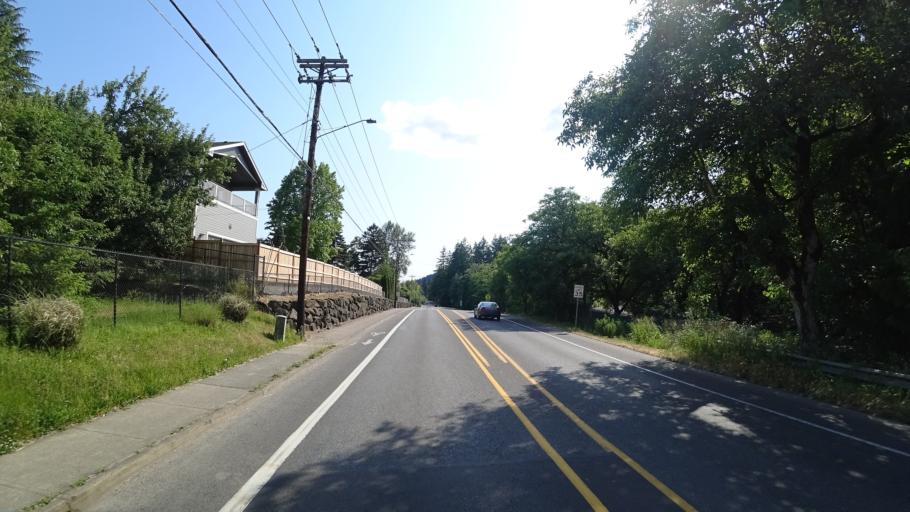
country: US
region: Oregon
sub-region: Clackamas County
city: Happy Valley
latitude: 45.4397
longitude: -122.5340
